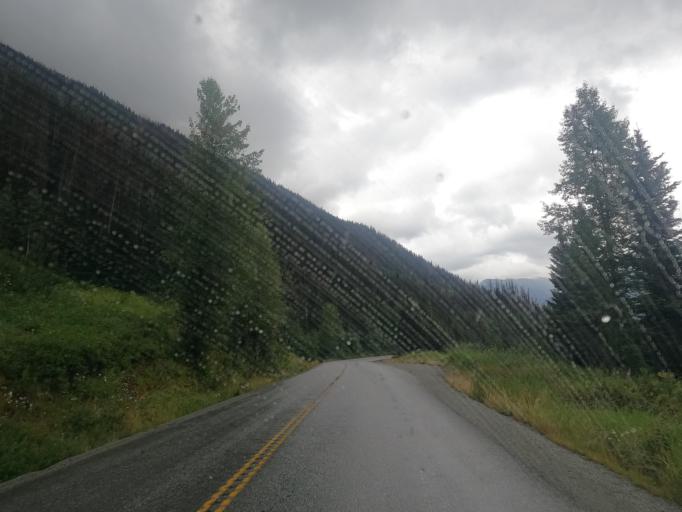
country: CA
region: British Columbia
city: Pemberton
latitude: 50.3845
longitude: -122.4302
